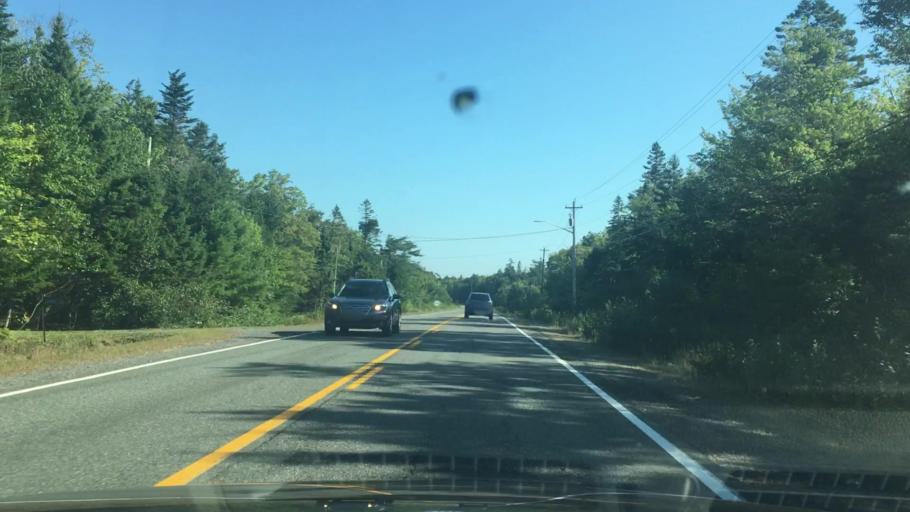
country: CA
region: Nova Scotia
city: Cole Harbour
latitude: 44.7984
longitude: -62.8848
